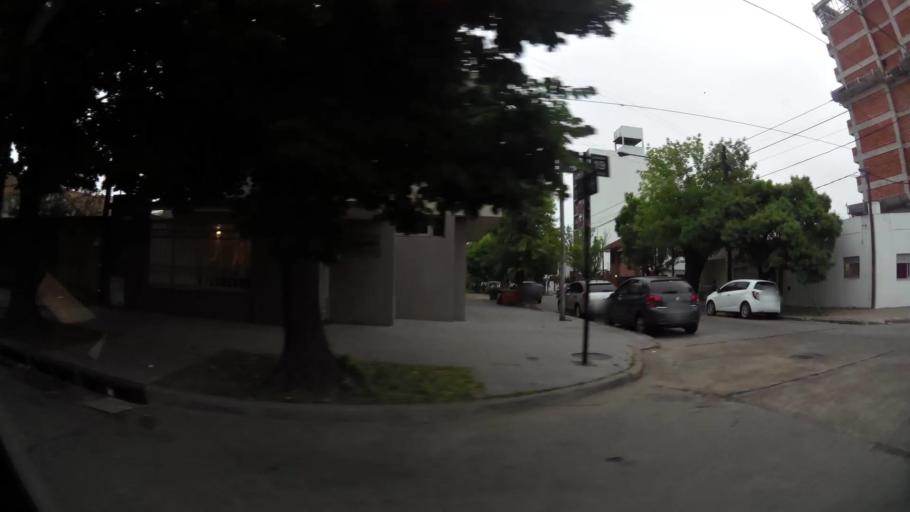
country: AR
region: Buenos Aires
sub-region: Partido de La Plata
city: La Plata
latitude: -34.9128
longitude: -57.9801
